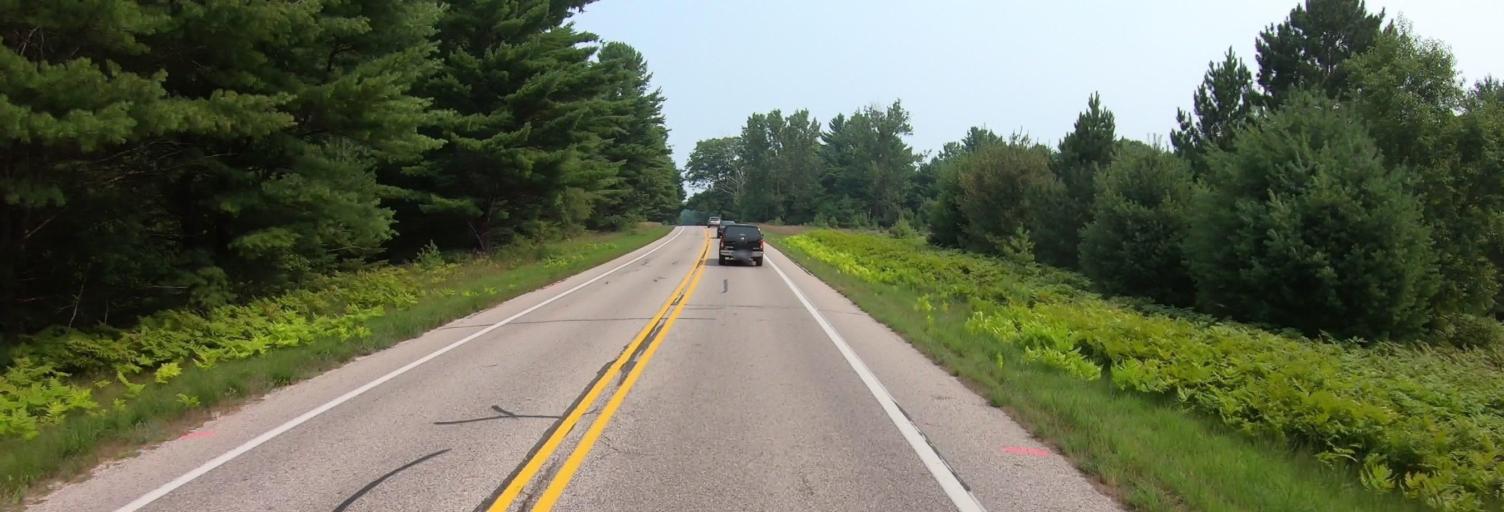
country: US
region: Michigan
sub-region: Leelanau County
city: Leland
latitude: 44.9208
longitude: -85.9522
